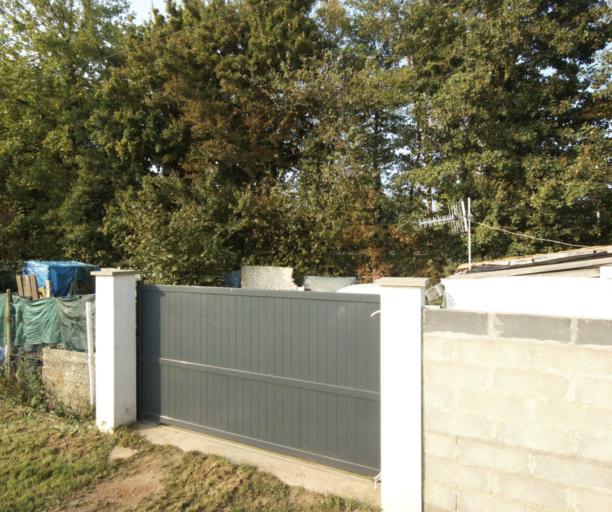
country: FR
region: Nord-Pas-de-Calais
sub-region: Departement du Nord
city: Haubourdin
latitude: 50.5974
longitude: 2.9859
